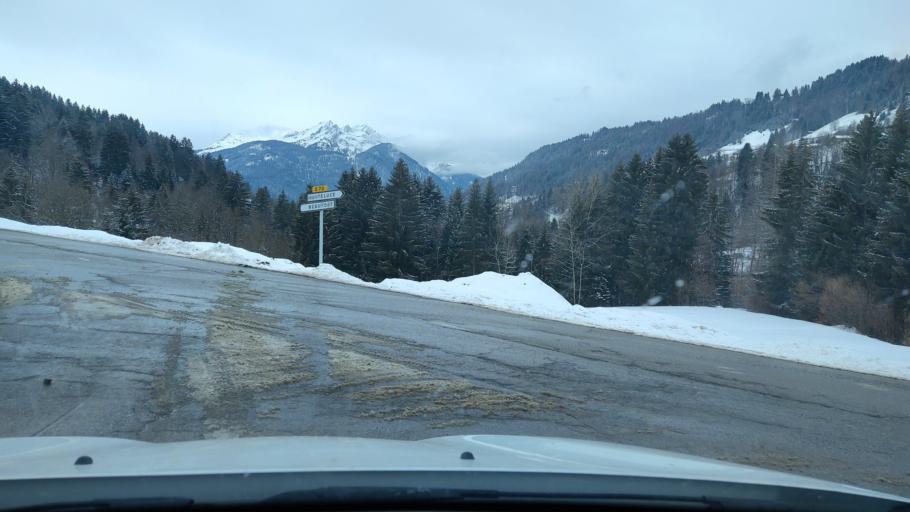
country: FR
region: Rhone-Alpes
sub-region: Departement de la Savoie
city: Beaufort
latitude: 45.7491
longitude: 6.5914
